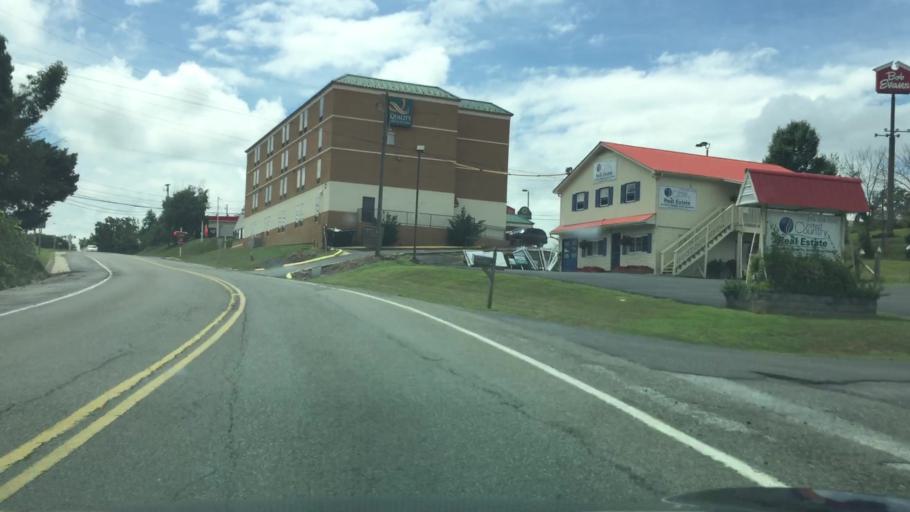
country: US
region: Virginia
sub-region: Wythe County
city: Wytheville
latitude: 36.9479
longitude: -81.0550
